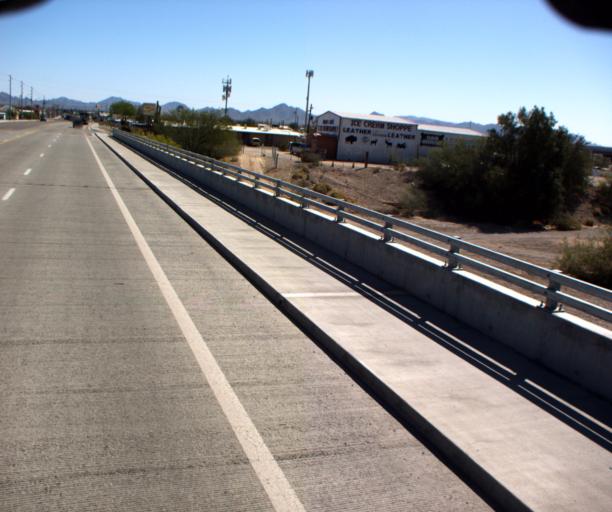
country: US
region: Arizona
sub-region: La Paz County
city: Quartzsite
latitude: 33.6661
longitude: -114.2215
